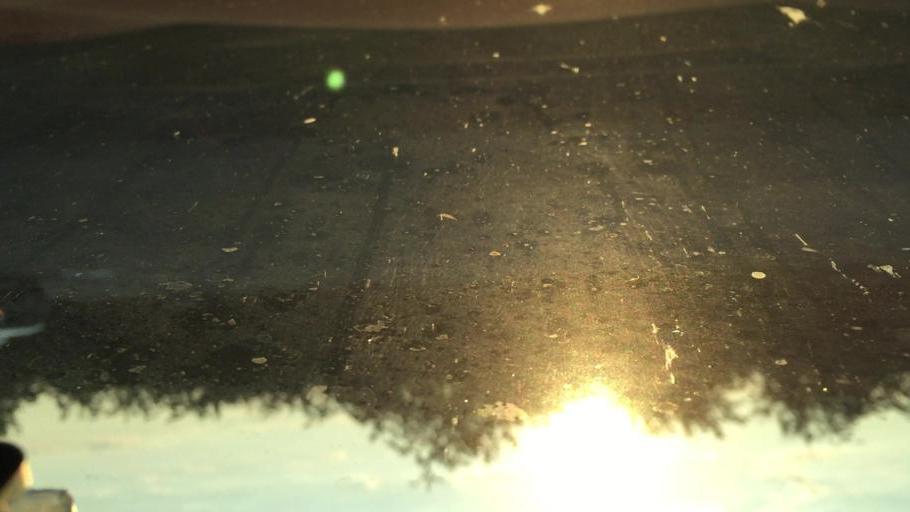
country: US
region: California
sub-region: San Joaquin County
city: Manteca
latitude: 37.7666
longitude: -121.2155
